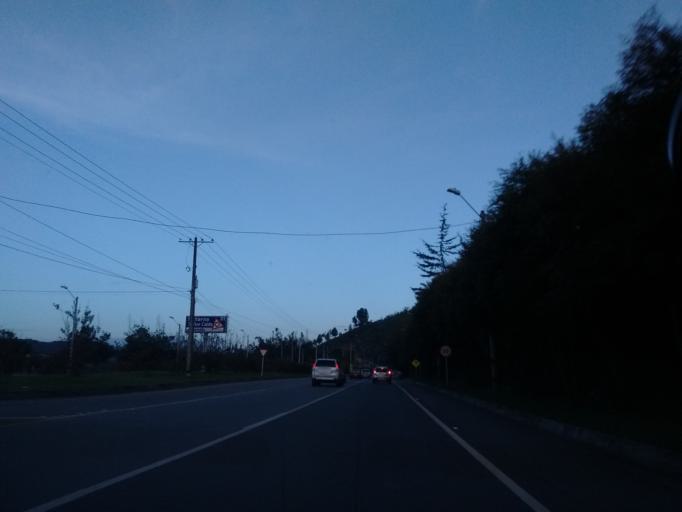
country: CO
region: Antioquia
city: Santuario
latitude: 6.1362
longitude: -75.2785
